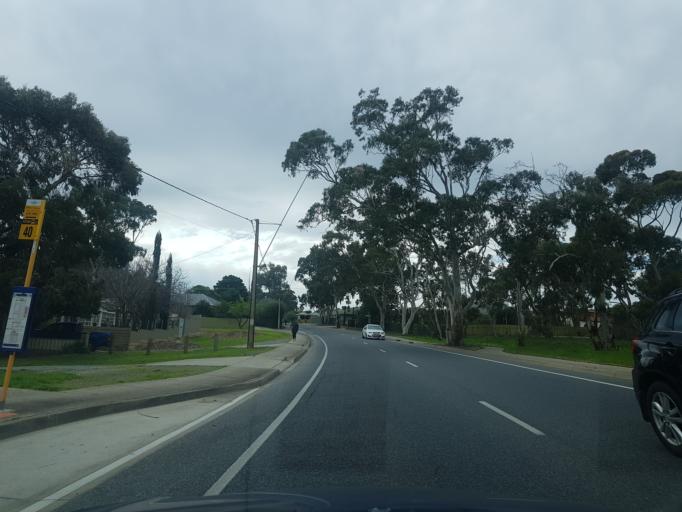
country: AU
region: South Australia
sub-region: Tea Tree Gully
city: Hope Valley
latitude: -34.8486
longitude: 138.7161
